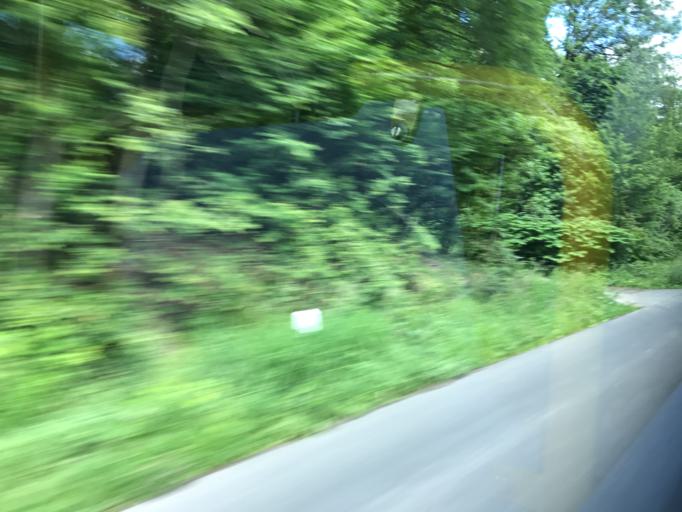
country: DE
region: Hesse
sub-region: Regierungsbezirk Darmstadt
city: Schlangenbad
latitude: 50.0804
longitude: 8.1089
